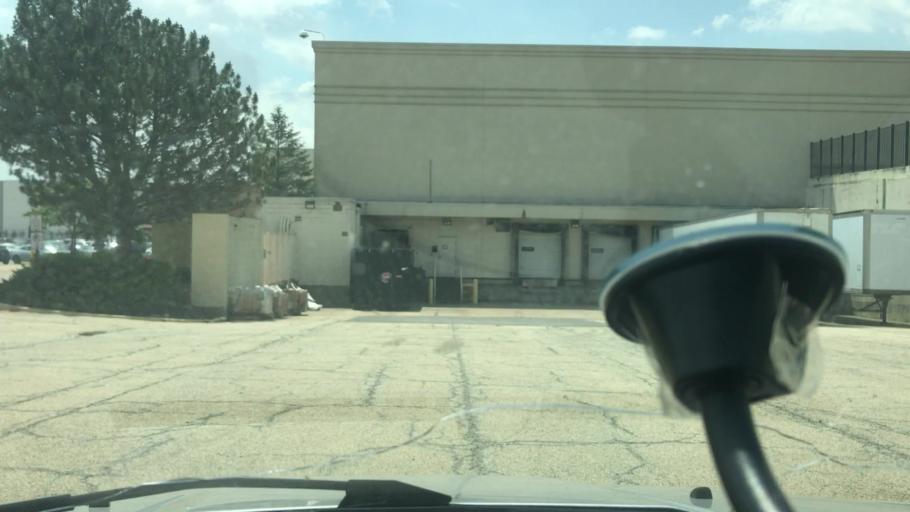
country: US
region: Illinois
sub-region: Peoria County
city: West Peoria
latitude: 40.7427
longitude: -89.6299
